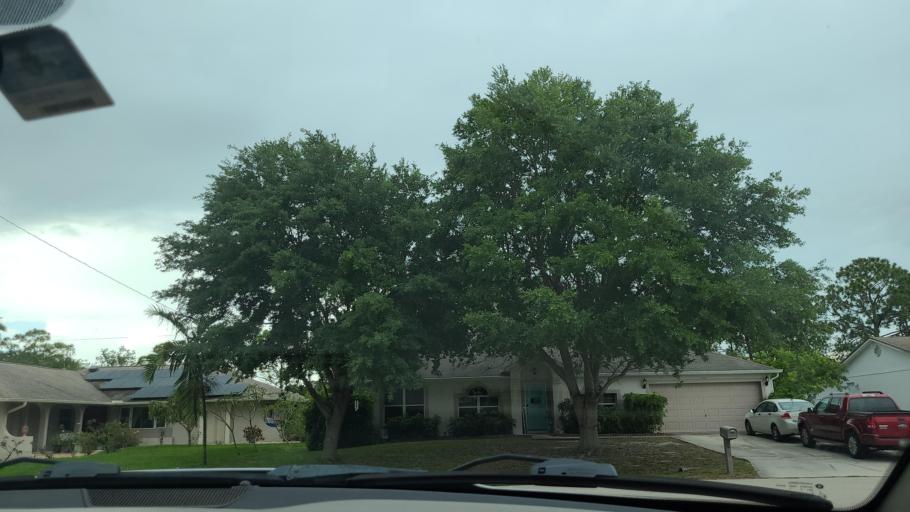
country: US
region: Florida
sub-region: Brevard County
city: West Melbourne
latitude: 28.0125
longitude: -80.6665
